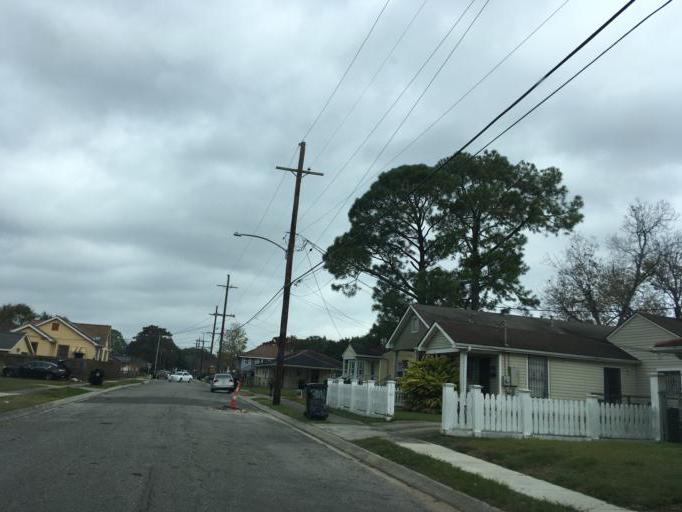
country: US
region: Louisiana
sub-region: Orleans Parish
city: New Orleans
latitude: 29.9931
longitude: -90.0575
